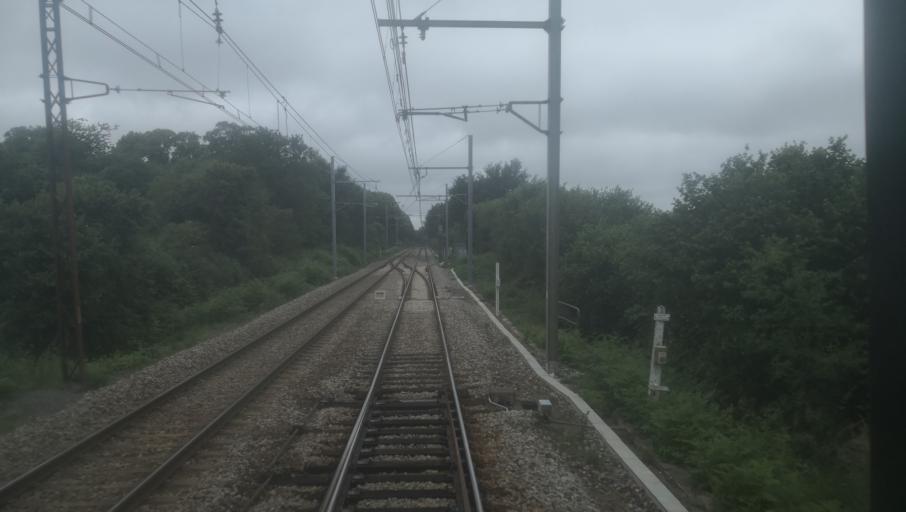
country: FR
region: Limousin
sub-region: Departement de la Creuse
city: La Souterraine
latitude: 46.2489
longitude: 1.4836
